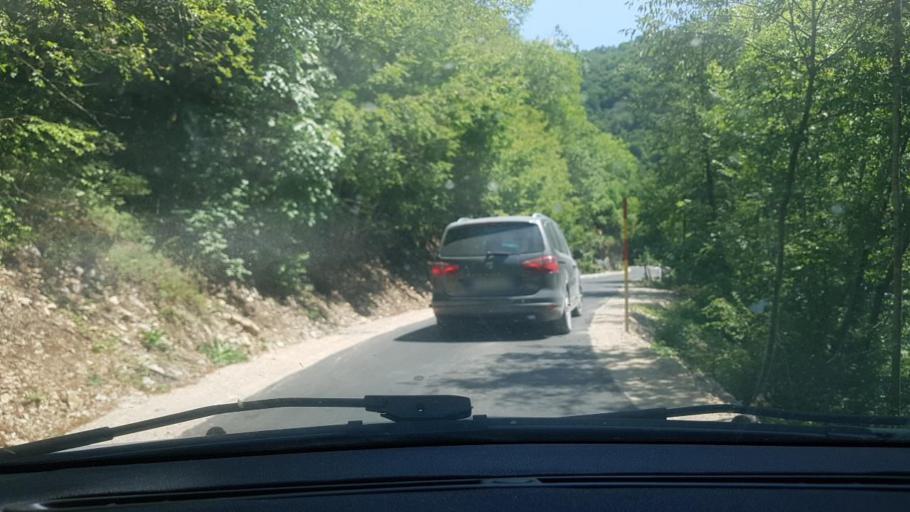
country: BA
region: Federation of Bosnia and Herzegovina
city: Orasac
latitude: 44.6262
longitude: 16.0468
